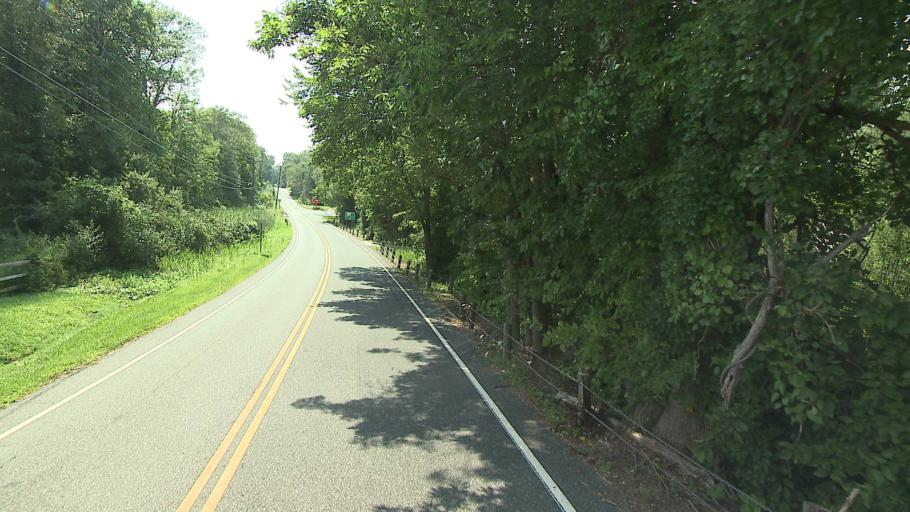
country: US
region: Connecticut
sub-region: Litchfield County
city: New Preston
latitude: 41.6531
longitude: -73.2875
